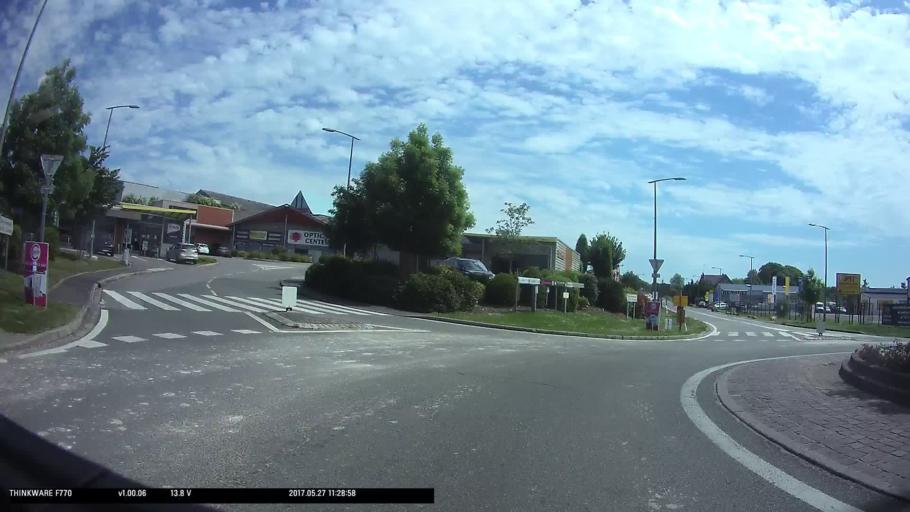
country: FR
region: Picardie
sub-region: Departement de l'Oise
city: Trie-Chateau
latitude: 49.2876
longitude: 1.8015
